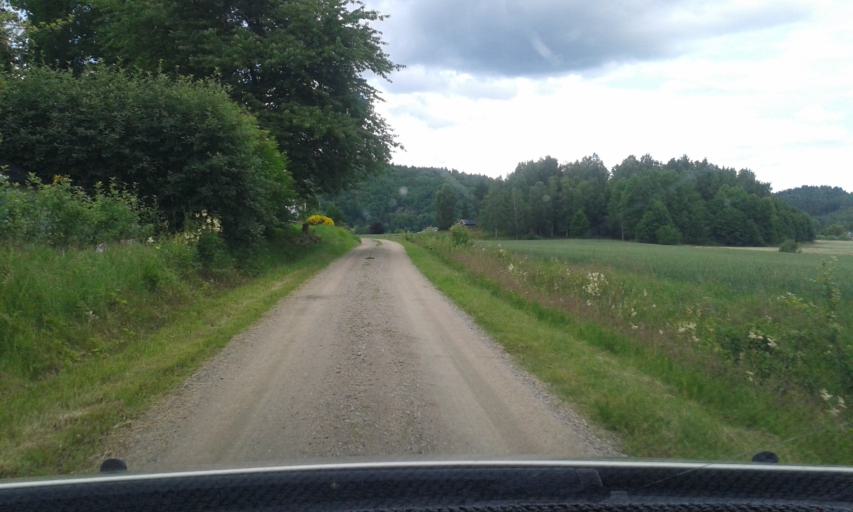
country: SE
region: Vaestra Goetaland
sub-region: Lilla Edets Kommun
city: Lilla Edet
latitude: 58.1380
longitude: 12.0884
